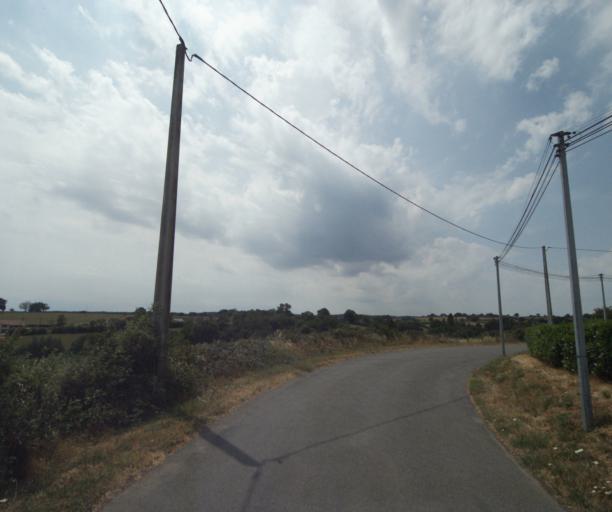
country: FR
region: Bourgogne
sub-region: Departement de Saone-et-Loire
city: Gueugnon
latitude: 46.5970
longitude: 4.0252
